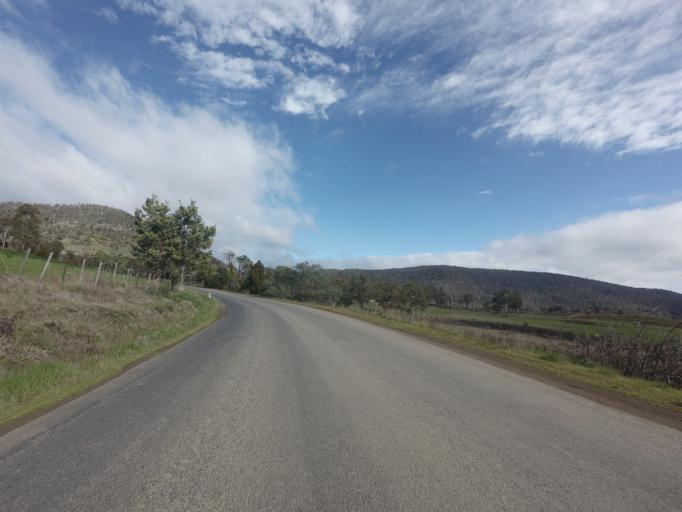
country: AU
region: Tasmania
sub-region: Derwent Valley
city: New Norfolk
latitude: -42.7761
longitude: 146.9718
